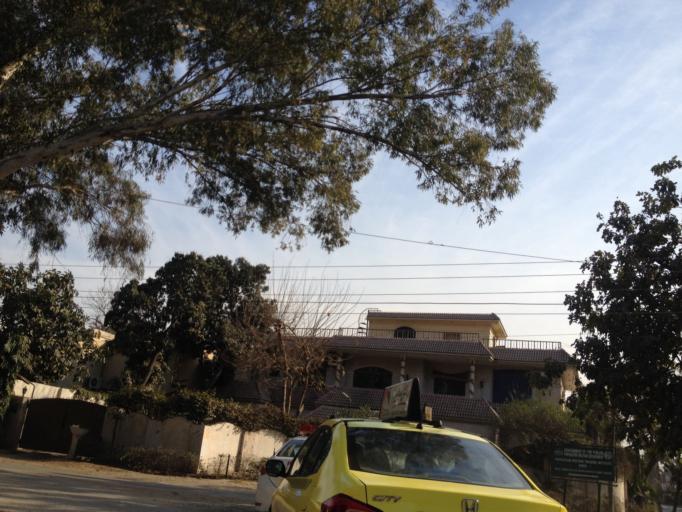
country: PK
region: Punjab
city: Lahore
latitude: 31.5061
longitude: 74.3187
